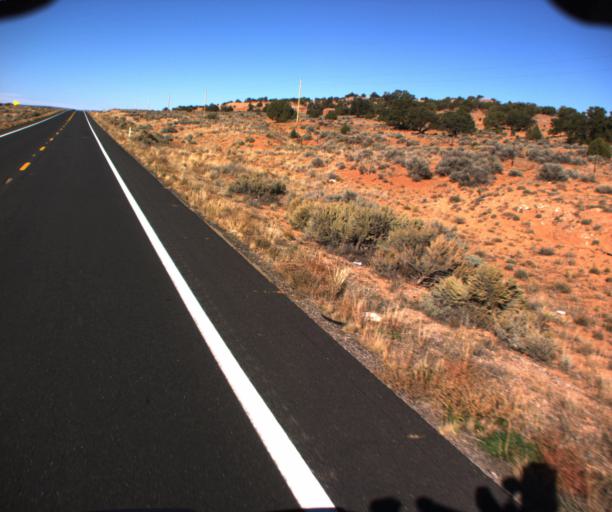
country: US
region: Arizona
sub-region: Coconino County
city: Kaibito
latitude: 36.5297
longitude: -110.7014
